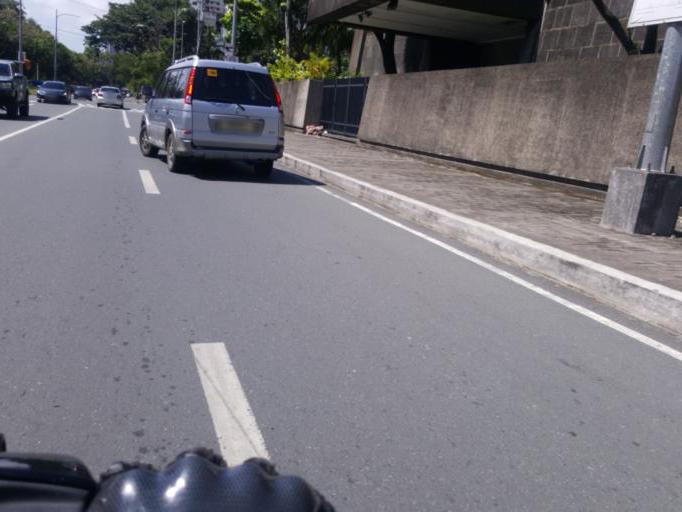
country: PH
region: Metro Manila
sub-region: City of Manila
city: Port Area
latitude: 14.5622
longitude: 120.9863
